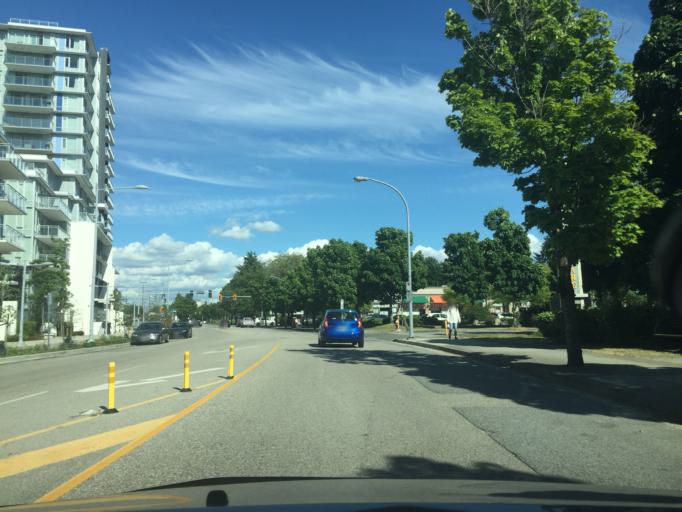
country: CA
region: British Columbia
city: Richmond
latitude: 49.1879
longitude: -123.1301
